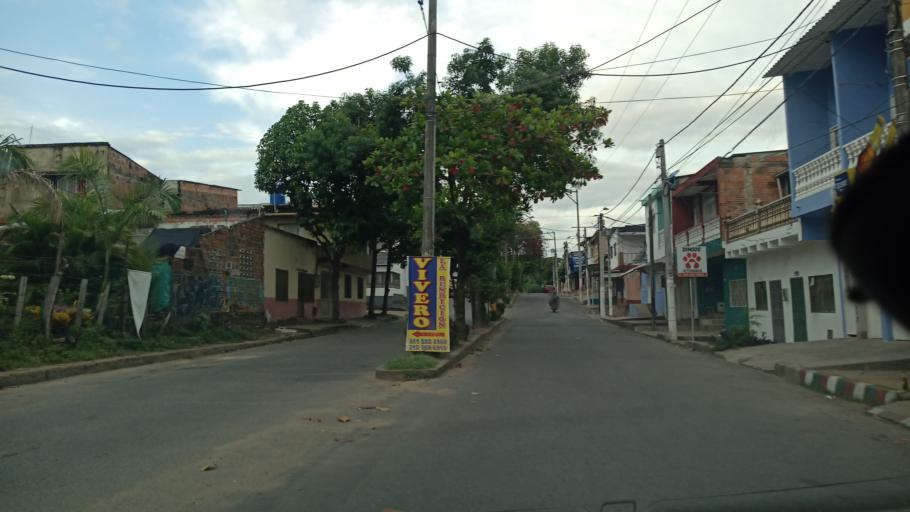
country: CO
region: Tolima
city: Melgar
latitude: 4.1989
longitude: -74.6508
